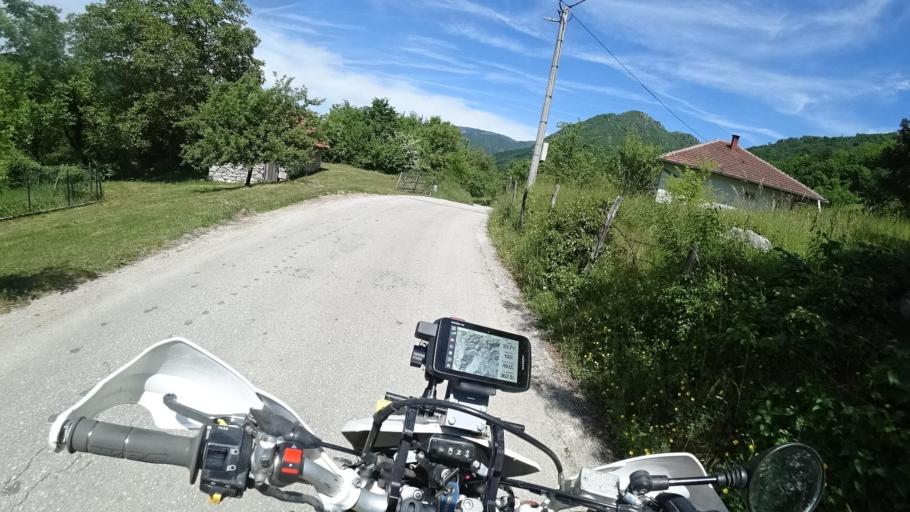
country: BA
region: Federation of Bosnia and Herzegovina
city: Bijela
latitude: 43.6152
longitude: 17.9592
